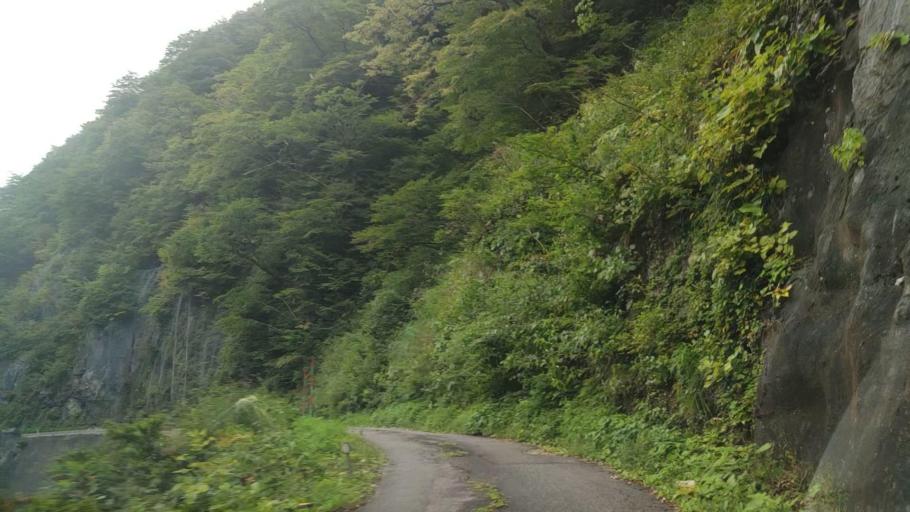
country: JP
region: Toyama
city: Yatsuomachi-higashikumisaka
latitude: 36.3912
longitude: 137.0801
